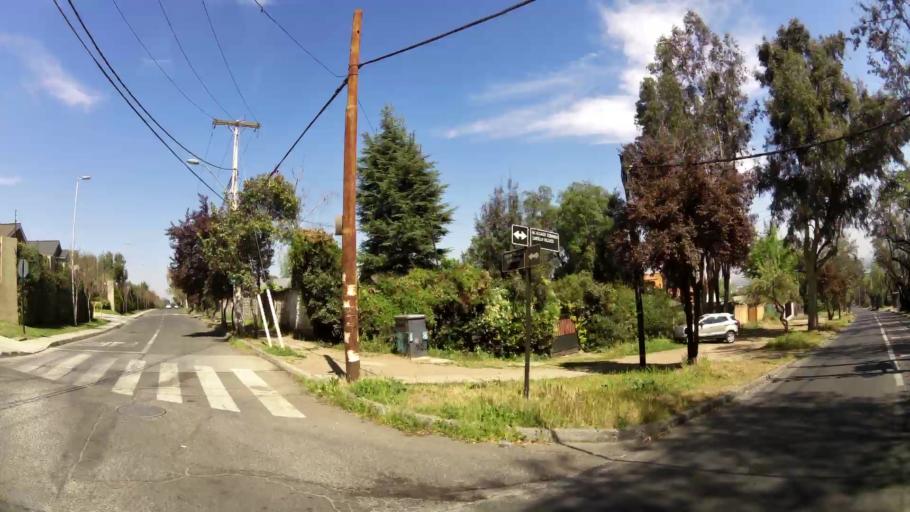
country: CL
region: Santiago Metropolitan
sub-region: Provincia de Santiago
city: Villa Presidente Frei, Nunoa, Santiago, Chile
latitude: -33.4532
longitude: -70.5245
